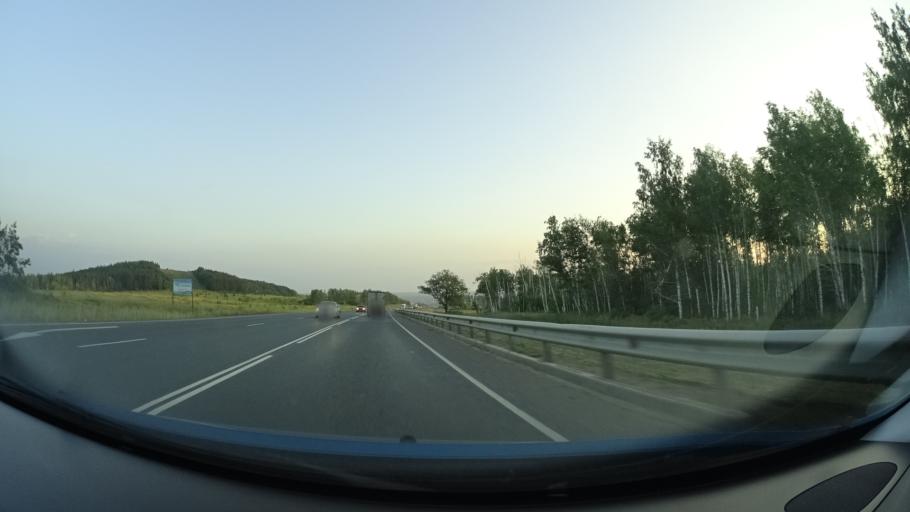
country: RU
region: Samara
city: Sernovodsk
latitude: 53.9150
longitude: 51.3026
